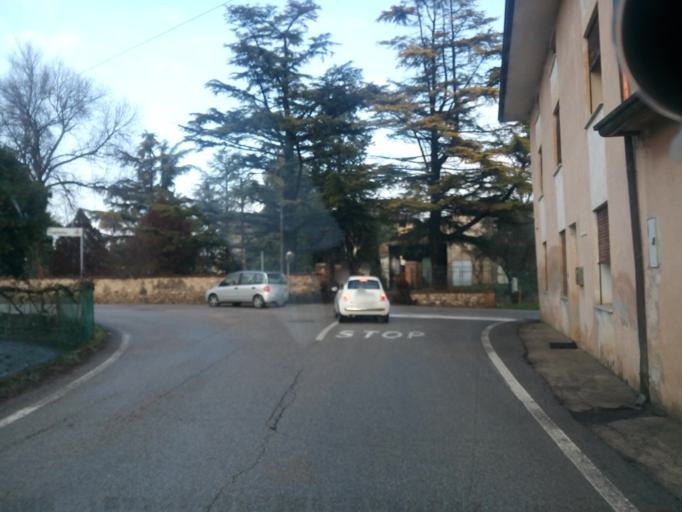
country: IT
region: Veneto
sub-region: Provincia di Vicenza
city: Breganze
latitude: 45.6877
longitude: 11.5767
